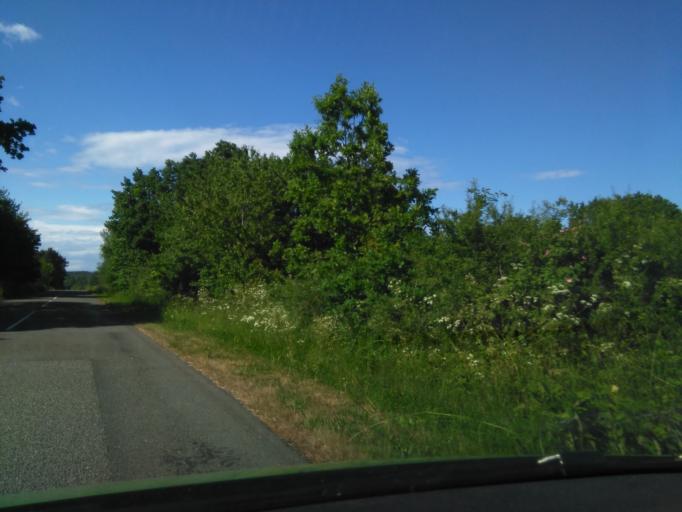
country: DK
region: Capital Region
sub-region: Bornholm Kommune
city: Nexo
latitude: 55.0706
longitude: 15.0822
